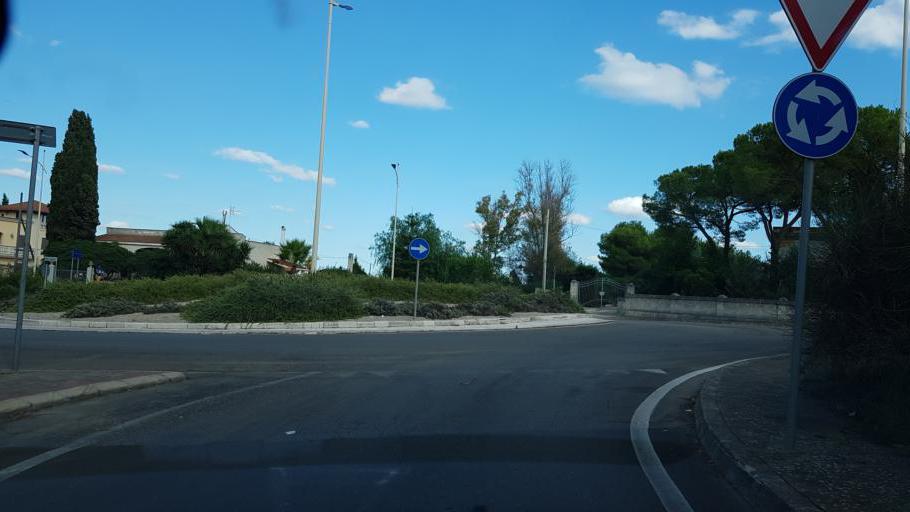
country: IT
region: Apulia
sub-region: Provincia di Lecce
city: Nardo
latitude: 40.1563
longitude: 18.0189
